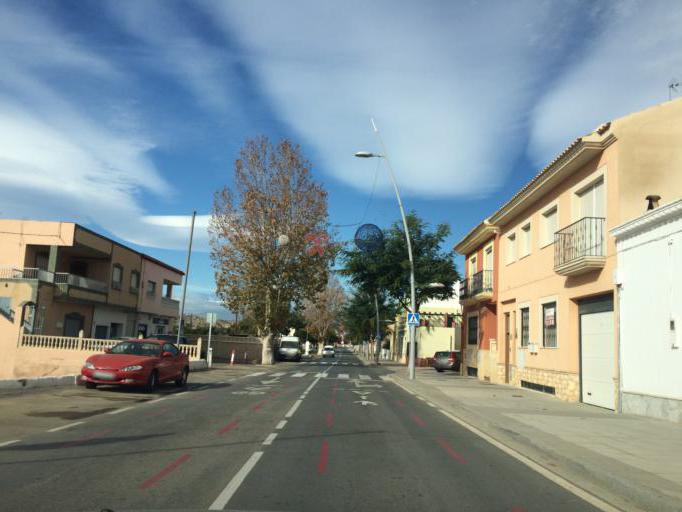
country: ES
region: Andalusia
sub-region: Provincia de Almeria
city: Rioja
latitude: 36.9463
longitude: -2.4658
